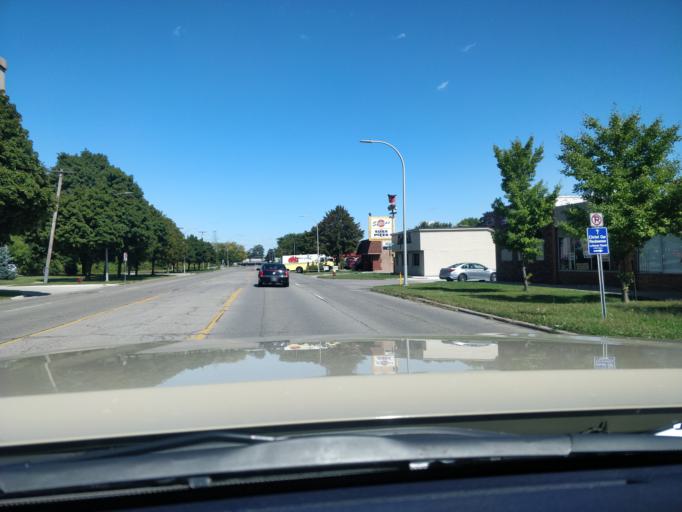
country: US
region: Michigan
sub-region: Wayne County
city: Allen Park
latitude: 42.2684
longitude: -83.1982
